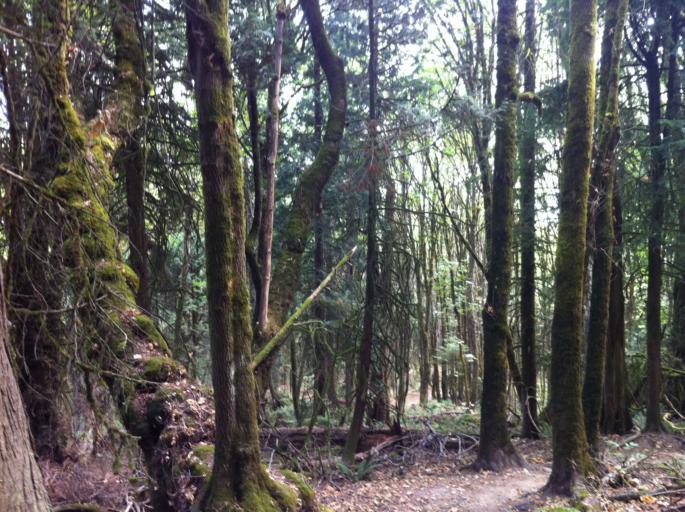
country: US
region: Oregon
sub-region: Clackamas County
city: Milwaukie
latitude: 45.4569
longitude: -122.6713
